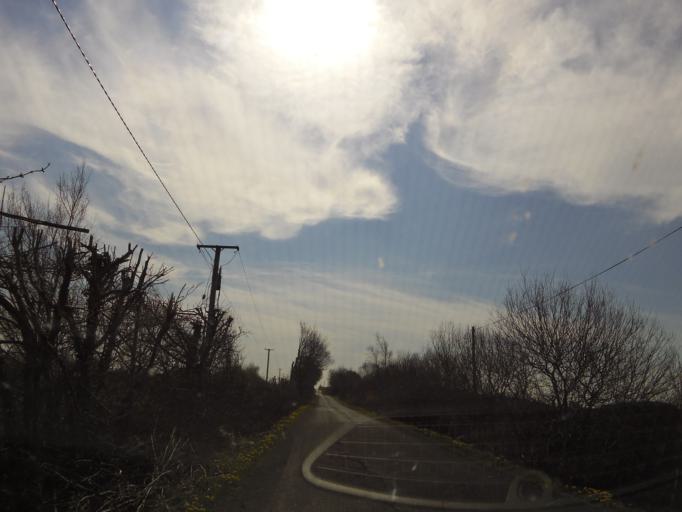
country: IE
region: Connaught
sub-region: Maigh Eo
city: Kiltamagh
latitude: 53.8367
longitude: -9.0021
